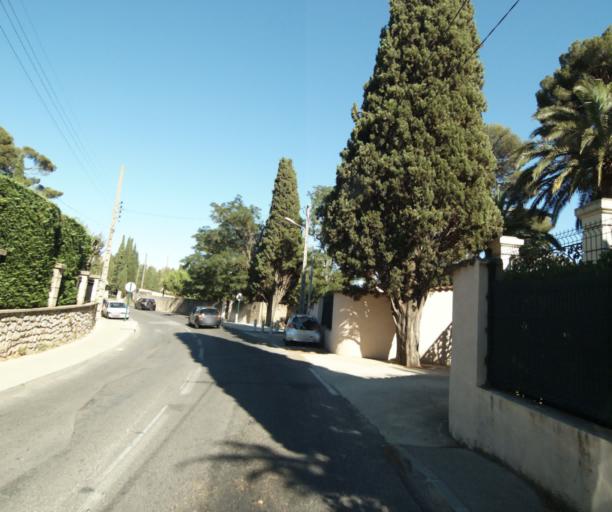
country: FR
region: Provence-Alpes-Cote d'Azur
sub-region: Departement du Var
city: La Garde
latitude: 43.1066
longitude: 5.9928
